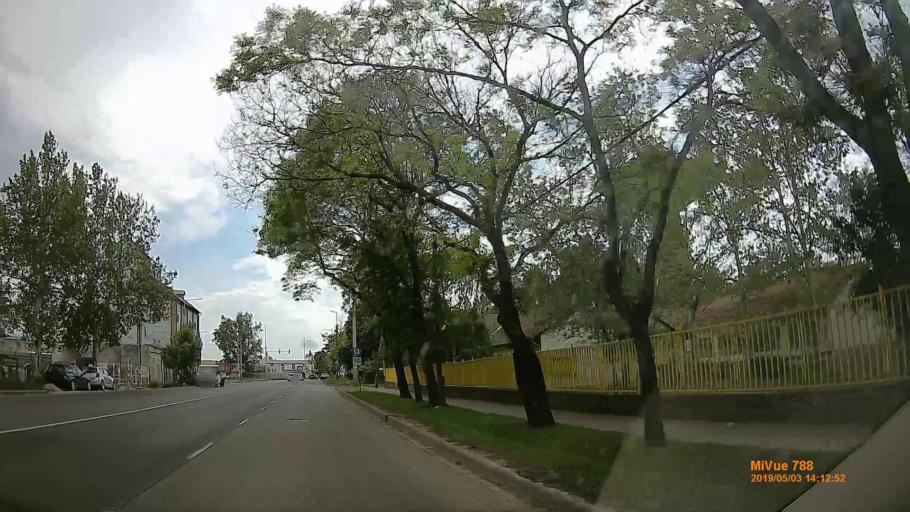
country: HU
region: Jasz-Nagykun-Szolnok
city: Szolnok
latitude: 47.1638
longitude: 20.1755
